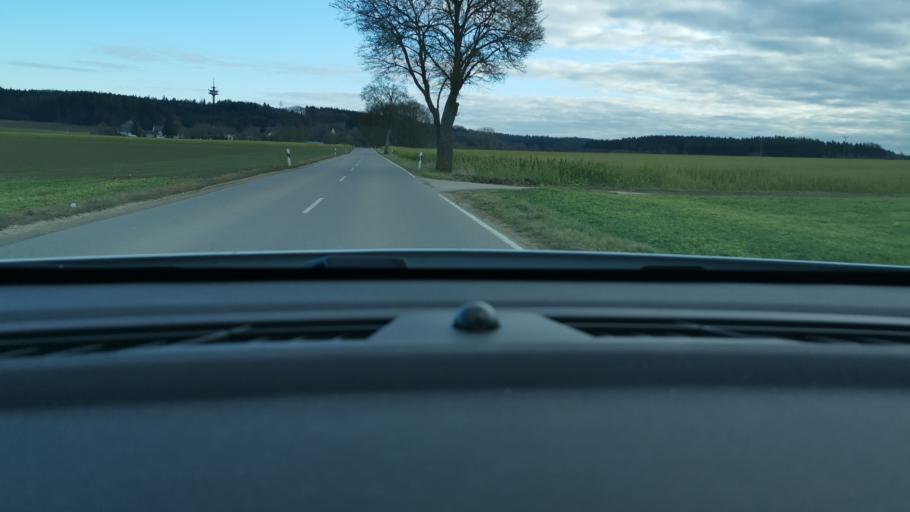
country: DE
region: Bavaria
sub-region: Swabia
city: Affing
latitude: 48.4957
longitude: 11.0039
